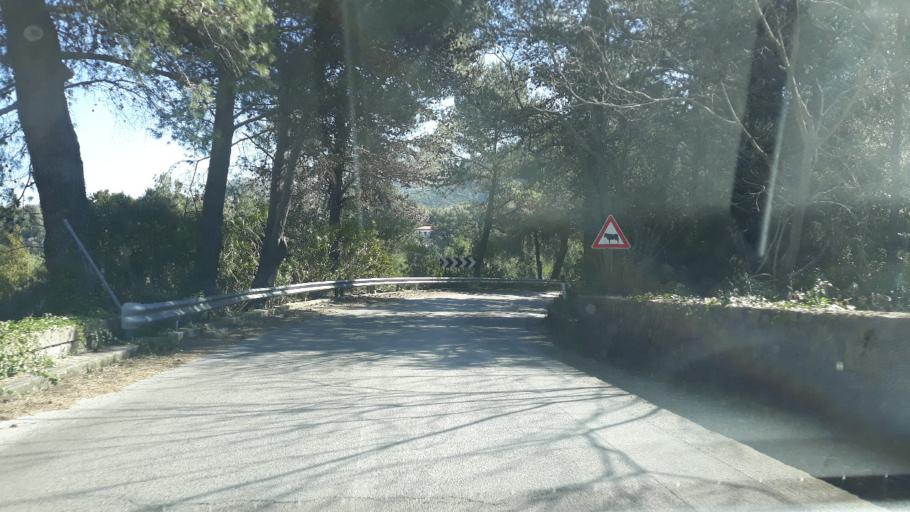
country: IT
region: Sicily
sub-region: Palermo
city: Piano dei Geli
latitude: 38.0923
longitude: 13.2578
